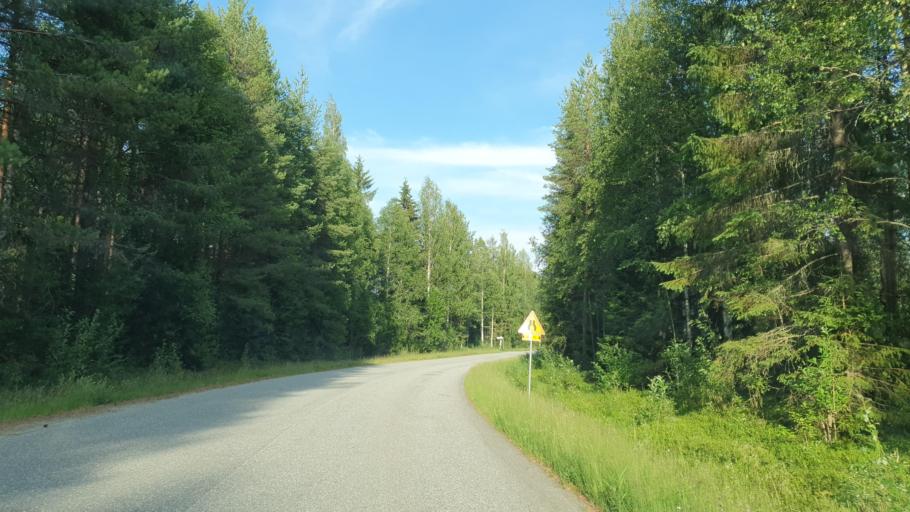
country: FI
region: Kainuu
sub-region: Kehys-Kainuu
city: Kuhmo
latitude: 64.3147
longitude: 29.5239
